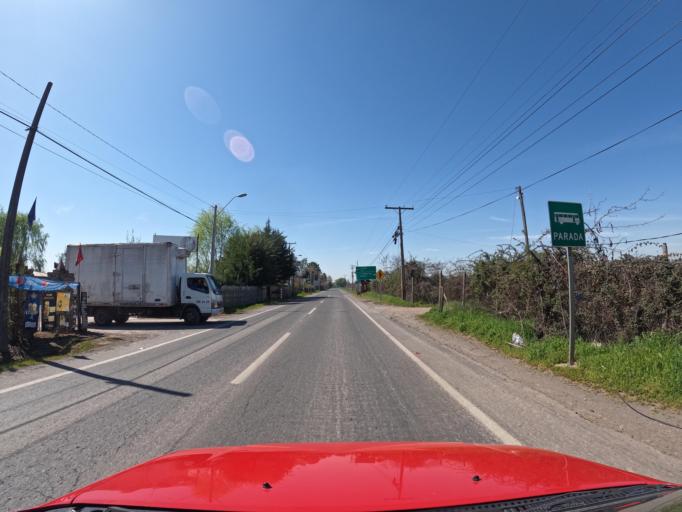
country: CL
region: Maule
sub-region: Provincia de Curico
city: Rauco
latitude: -34.9959
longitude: -71.3605
